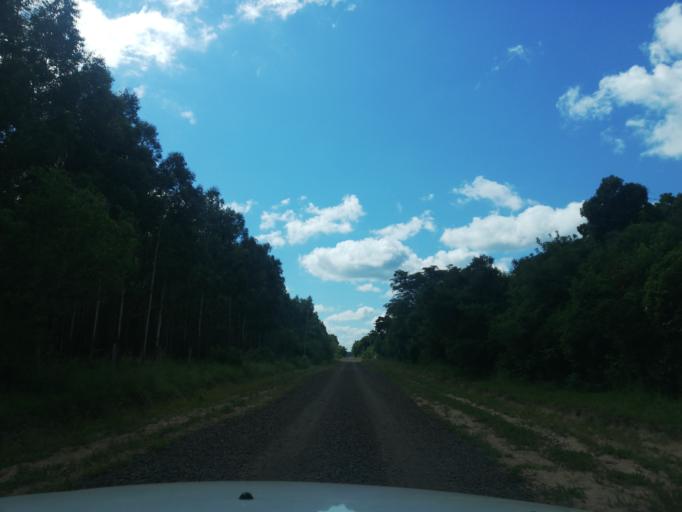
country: AR
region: Corrientes
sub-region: Departamento de San Miguel
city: San Miguel
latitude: -27.9871
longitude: -57.5414
